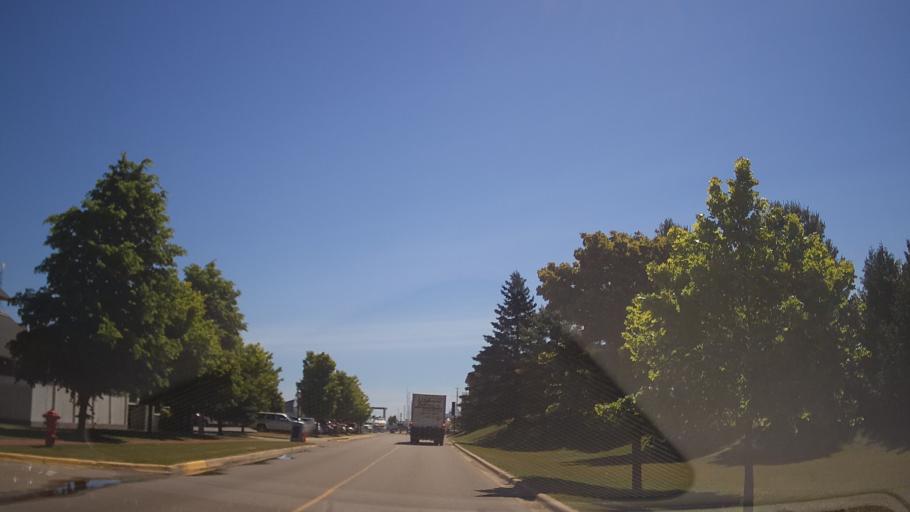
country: US
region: Michigan
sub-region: Mackinac County
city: Saint Ignace
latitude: 45.7799
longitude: -84.7278
